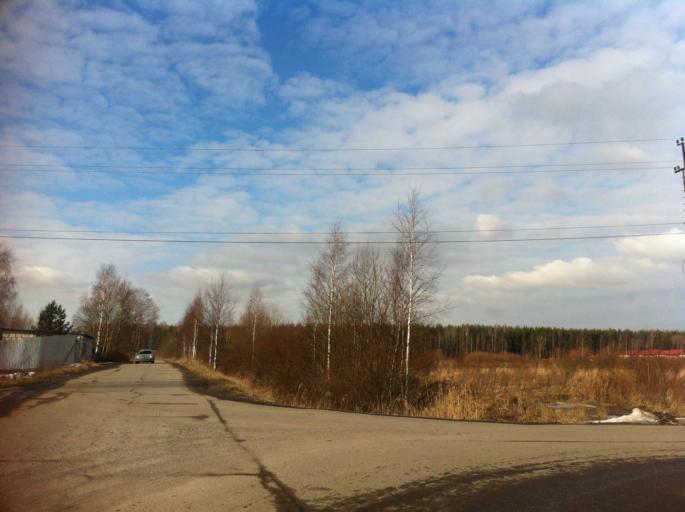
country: RU
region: Leningrad
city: Yanino Vtoroye
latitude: 59.9580
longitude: 30.5702
